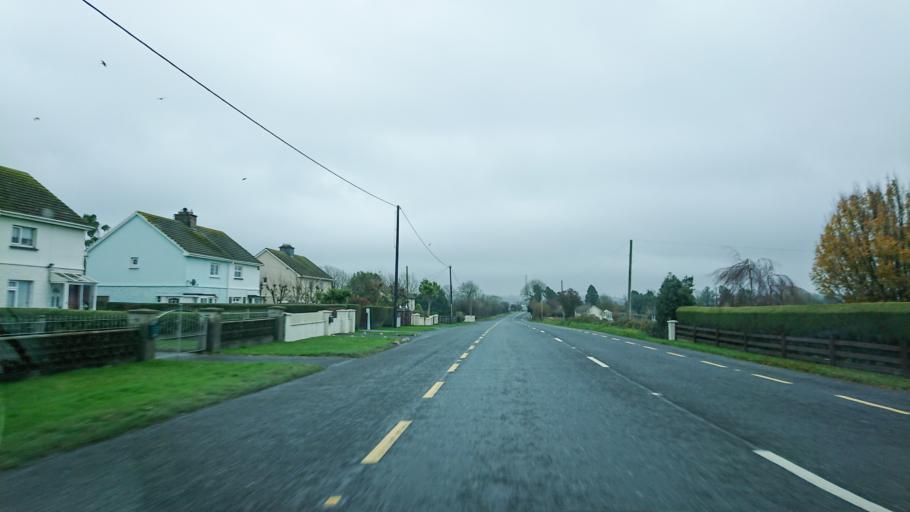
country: IE
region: Leinster
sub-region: Kilkenny
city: Mooncoin
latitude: 52.2821
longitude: -7.1787
